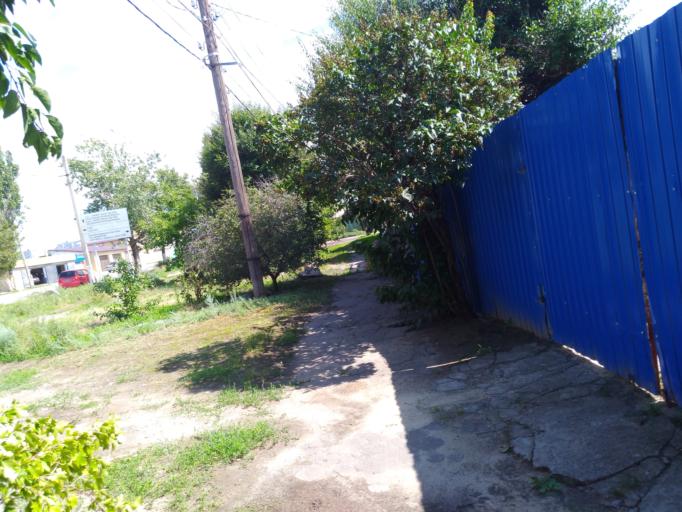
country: RU
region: Volgograd
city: Volgograd
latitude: 48.7053
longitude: 44.4785
